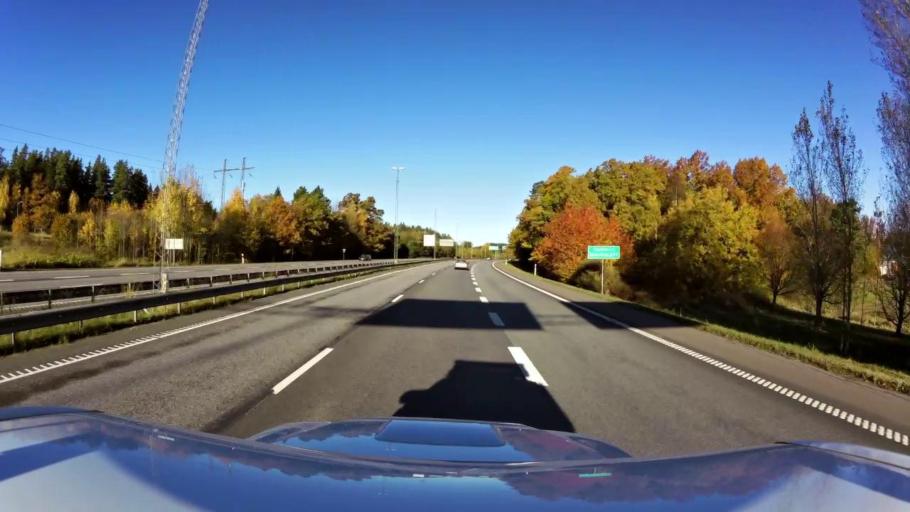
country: SE
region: OEstergoetland
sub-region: Linkopings Kommun
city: Malmslatt
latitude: 58.4073
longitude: 15.5524
